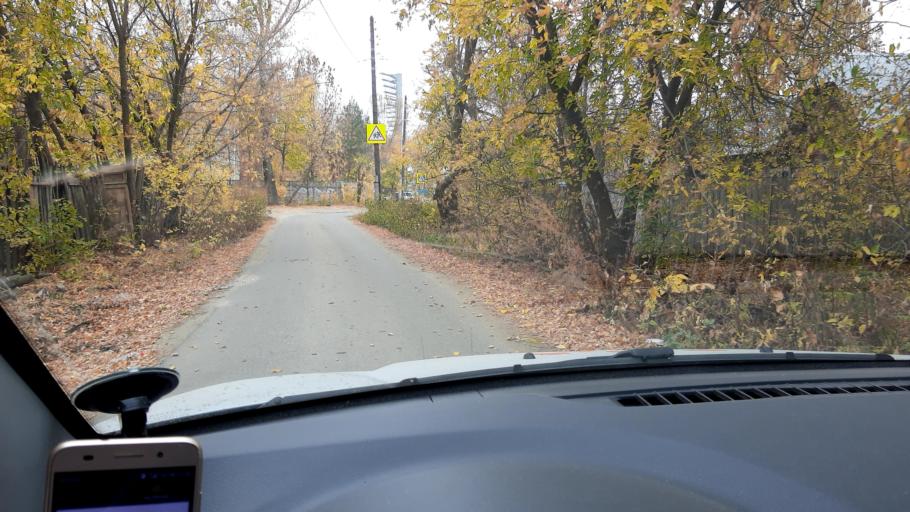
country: RU
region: Nizjnij Novgorod
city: Nizhniy Novgorod
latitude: 56.3130
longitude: 43.9274
